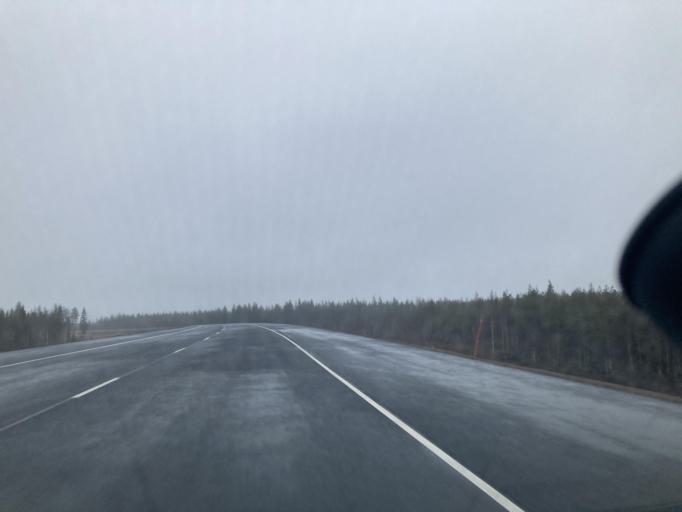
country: FI
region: Lapland
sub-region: Rovaniemi
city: Rovaniemi
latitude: 66.5851
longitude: 25.8012
